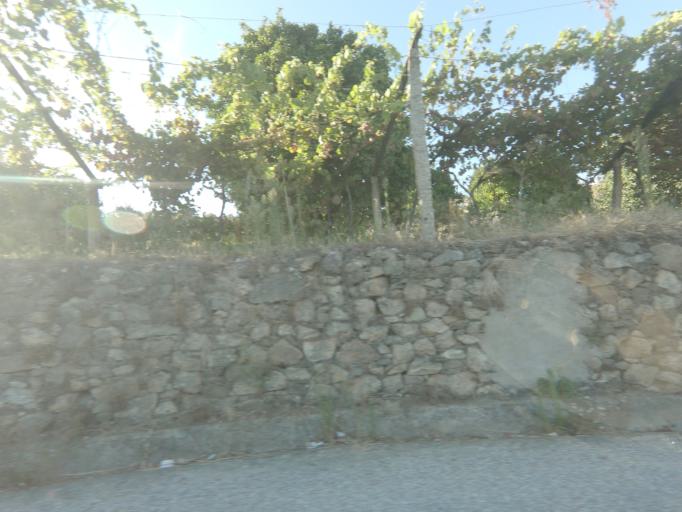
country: PT
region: Vila Real
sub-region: Peso da Regua
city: Godim
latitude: 41.1591
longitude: -7.8128
